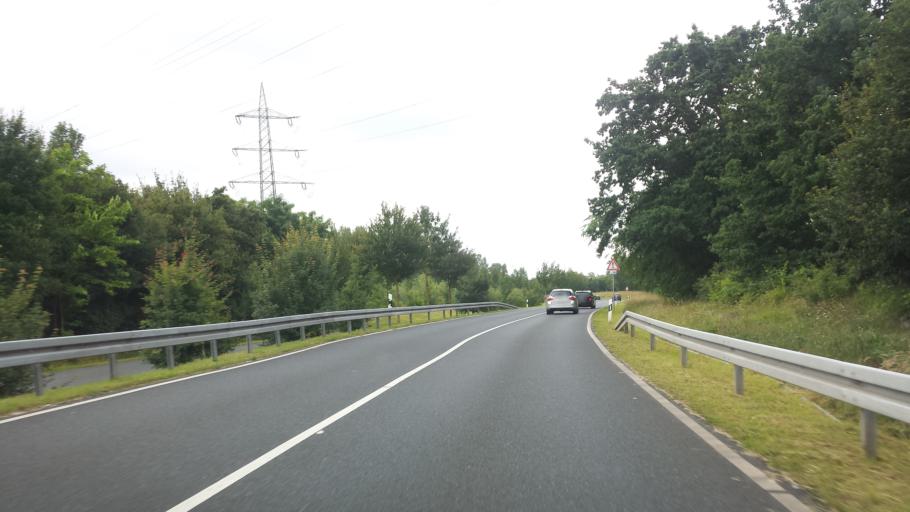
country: DE
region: Hesse
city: Kelsterbach
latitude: 50.0898
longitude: 8.5536
